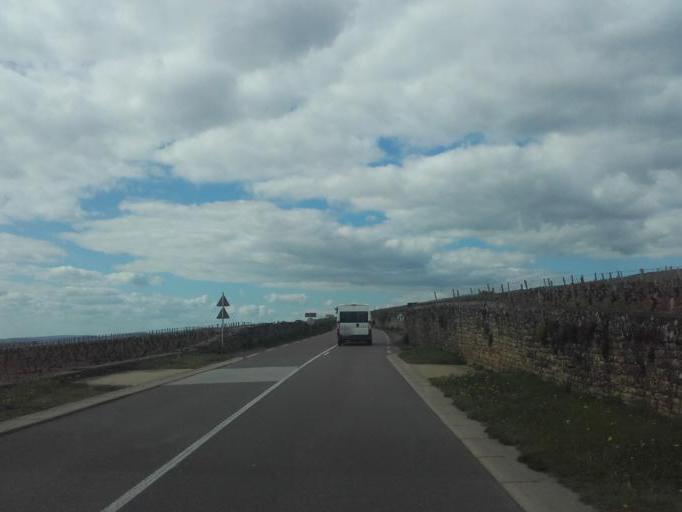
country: FR
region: Bourgogne
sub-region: Departement de la Cote-d'Or
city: Meursault
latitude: 46.9984
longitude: 4.7835
